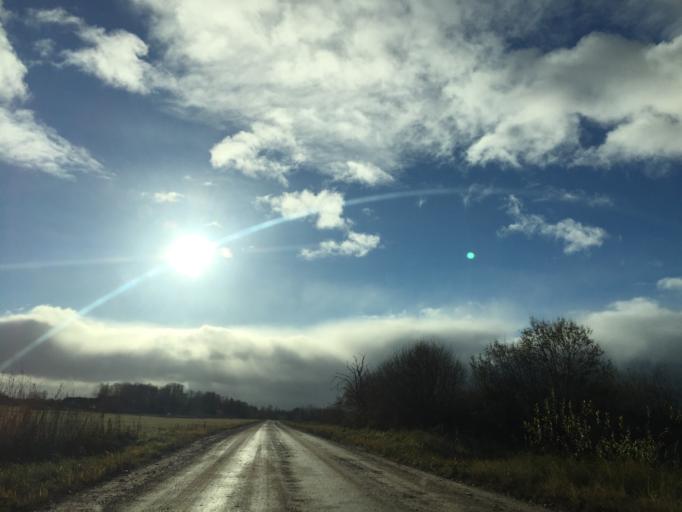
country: LV
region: Tukuma Rajons
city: Tukums
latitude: 56.9736
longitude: 22.9653
